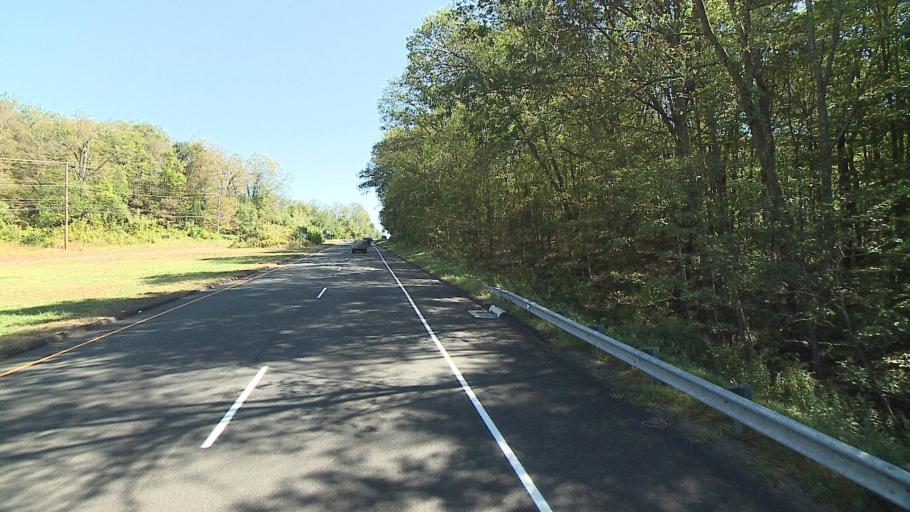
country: US
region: Connecticut
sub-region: Hartford County
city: Collinsville
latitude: 41.8328
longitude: -72.9227
